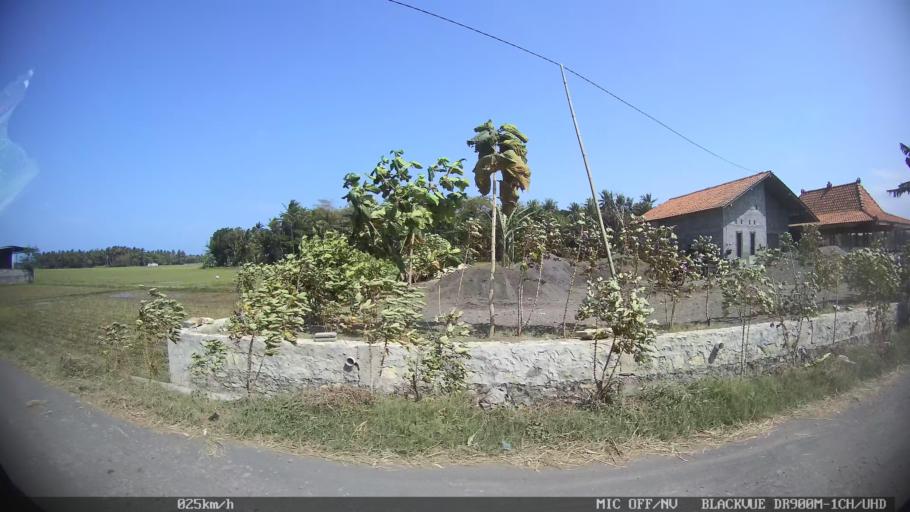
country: ID
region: Daerah Istimewa Yogyakarta
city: Srandakan
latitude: -7.9601
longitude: 110.2154
